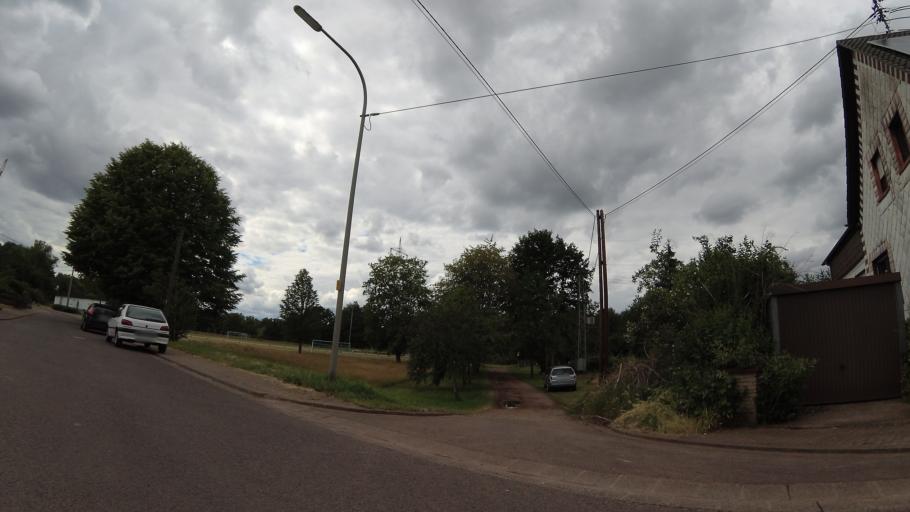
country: DE
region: Saarland
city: Saarwellingen
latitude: 49.3819
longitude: 6.8127
